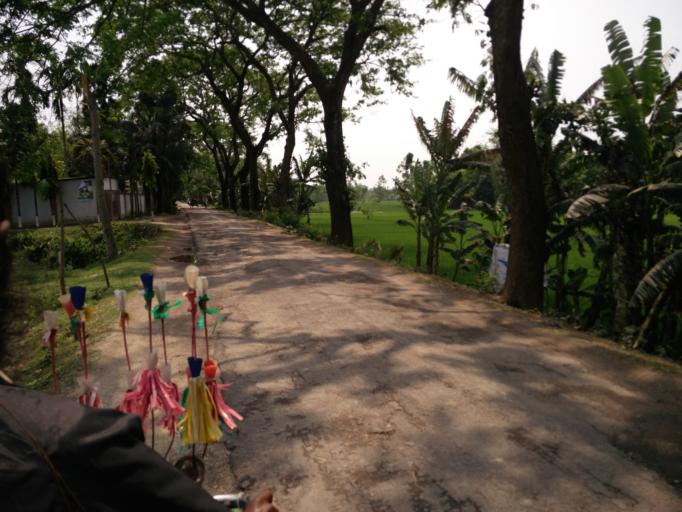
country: BD
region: Dhaka
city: Sherpur
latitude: 24.9411
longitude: 90.1600
